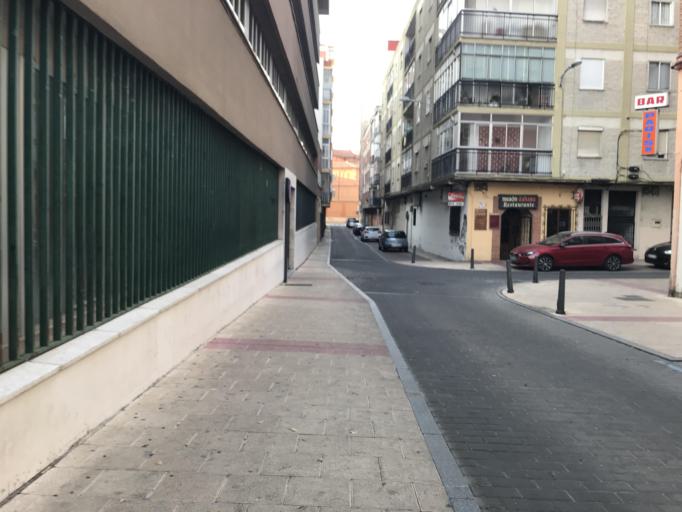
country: ES
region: Castille and Leon
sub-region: Provincia de Valladolid
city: Valladolid
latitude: 41.6556
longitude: -4.7207
